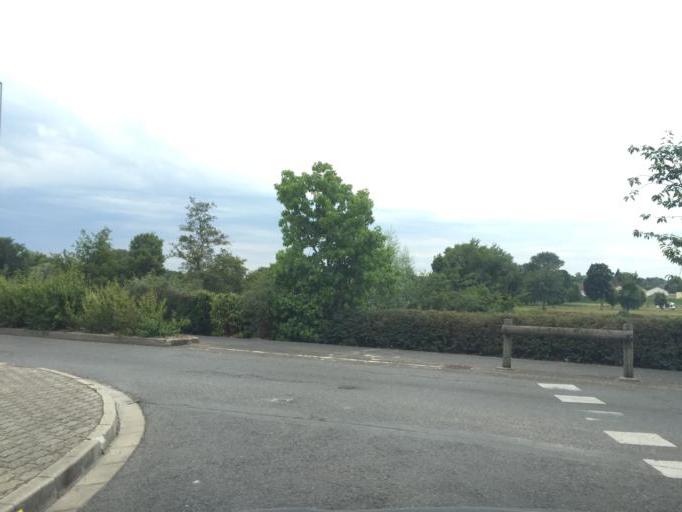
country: FR
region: Auvergne
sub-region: Departement de l'Allier
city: Moulins
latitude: 46.5608
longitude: 3.3266
